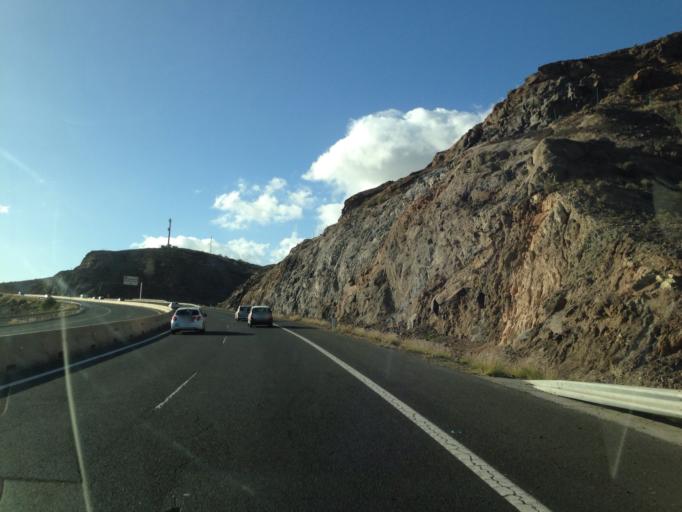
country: ES
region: Canary Islands
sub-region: Provincia de Las Palmas
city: Maspalomas
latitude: 27.7710
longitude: -15.6362
